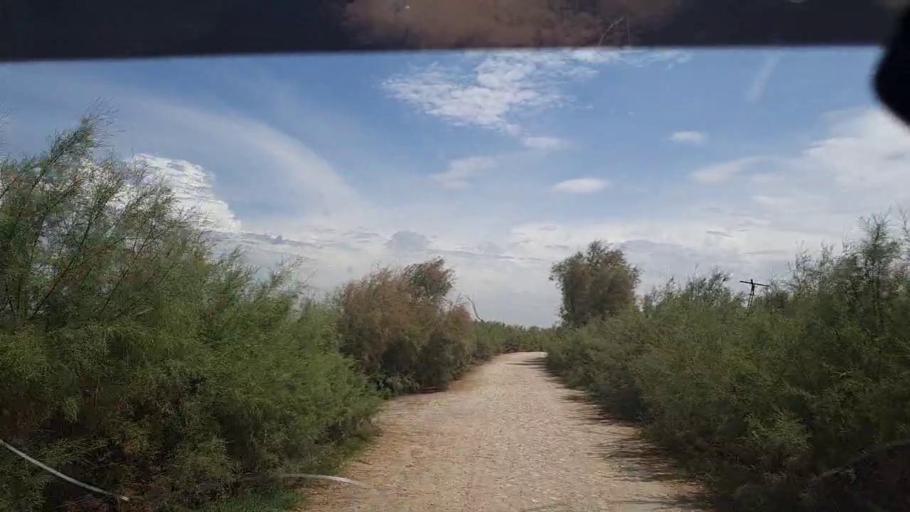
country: PK
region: Sindh
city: Ghauspur
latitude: 28.1449
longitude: 68.9778
